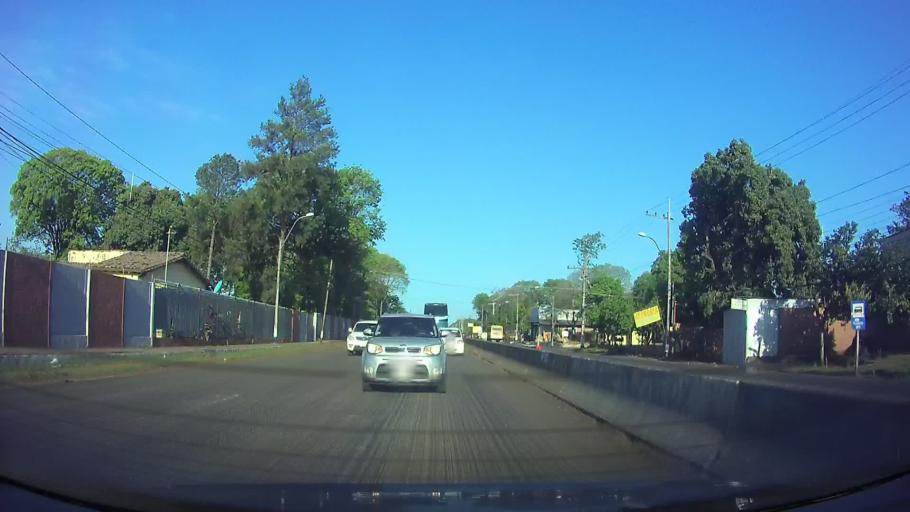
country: PY
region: Central
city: Capiata
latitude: -25.3468
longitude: -57.4737
